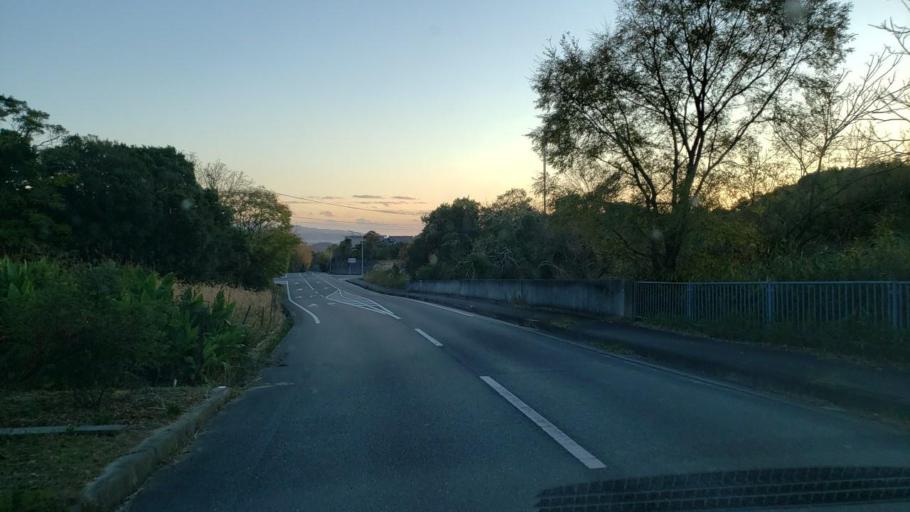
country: JP
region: Hyogo
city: Fukura
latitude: 34.3519
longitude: 134.7836
